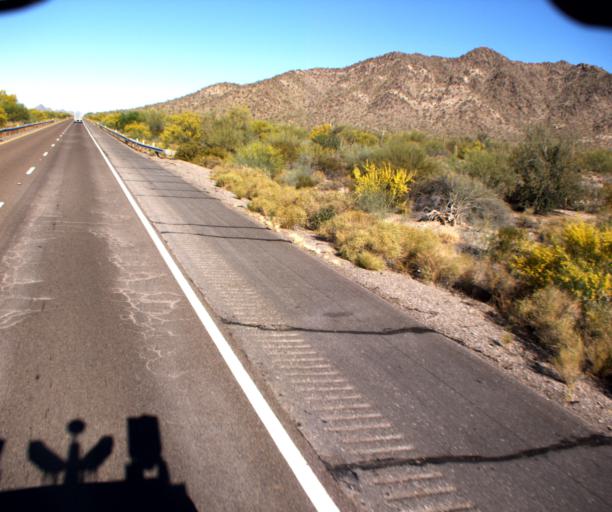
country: US
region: Arizona
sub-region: Maricopa County
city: Gila Bend
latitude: 32.8601
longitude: -112.3932
